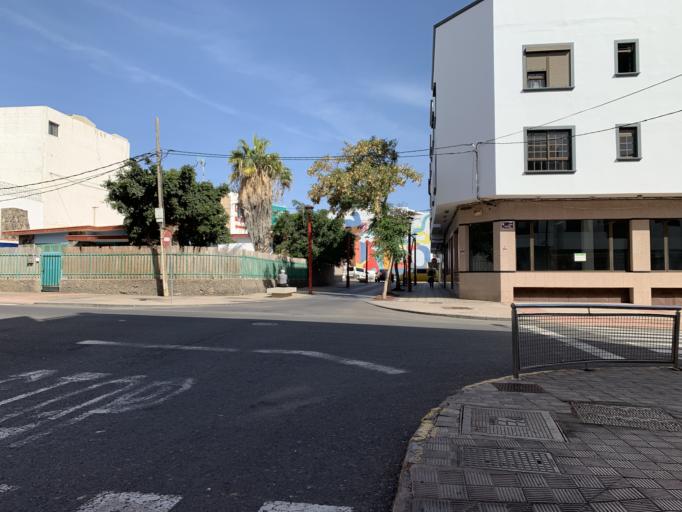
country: ES
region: Canary Islands
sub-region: Provincia de Las Palmas
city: Puerto del Rosario
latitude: 28.5004
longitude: -13.8669
